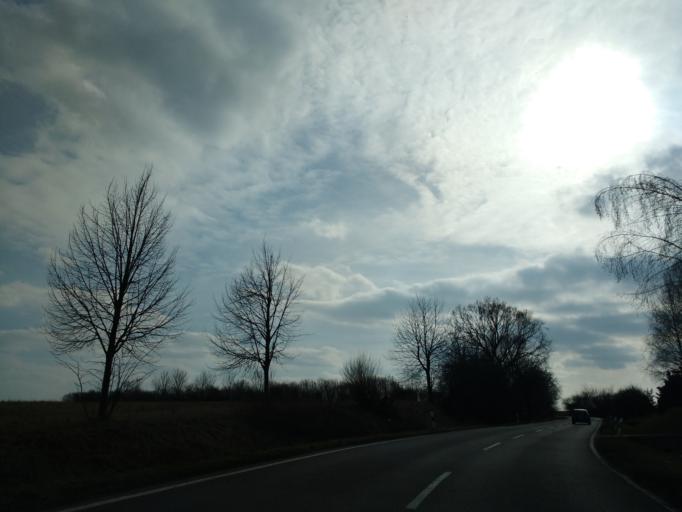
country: DE
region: Saxony-Anhalt
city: Schraplau
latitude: 51.4307
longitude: 11.6511
